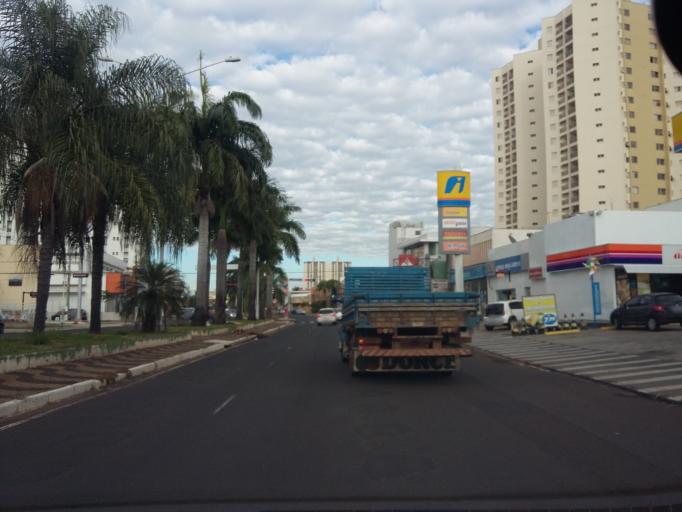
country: BR
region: Sao Paulo
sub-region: Sao Jose Do Rio Preto
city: Sao Jose do Rio Preto
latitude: -20.8151
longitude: -49.3921
